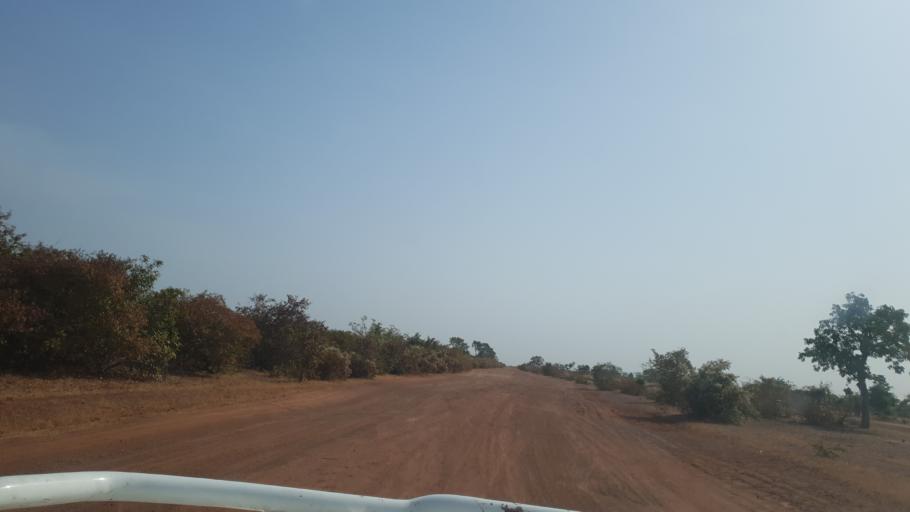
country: ML
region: Koulikoro
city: Dioila
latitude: 12.6697
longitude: -6.6599
